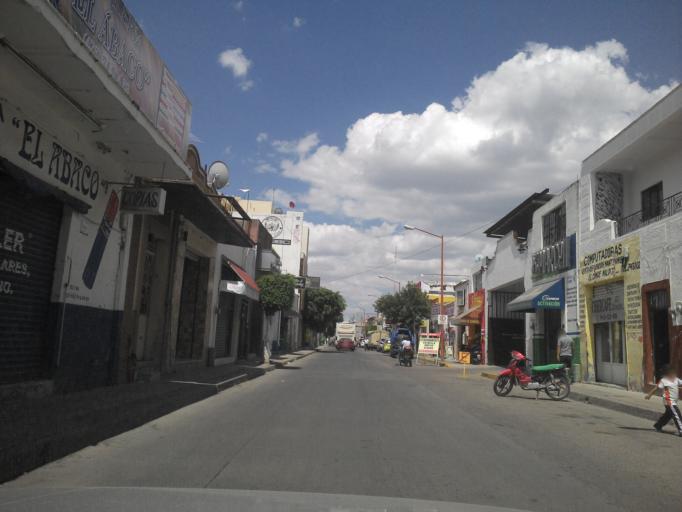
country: MX
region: Guanajuato
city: San Francisco del Rincon
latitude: 21.0174
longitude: -101.8568
